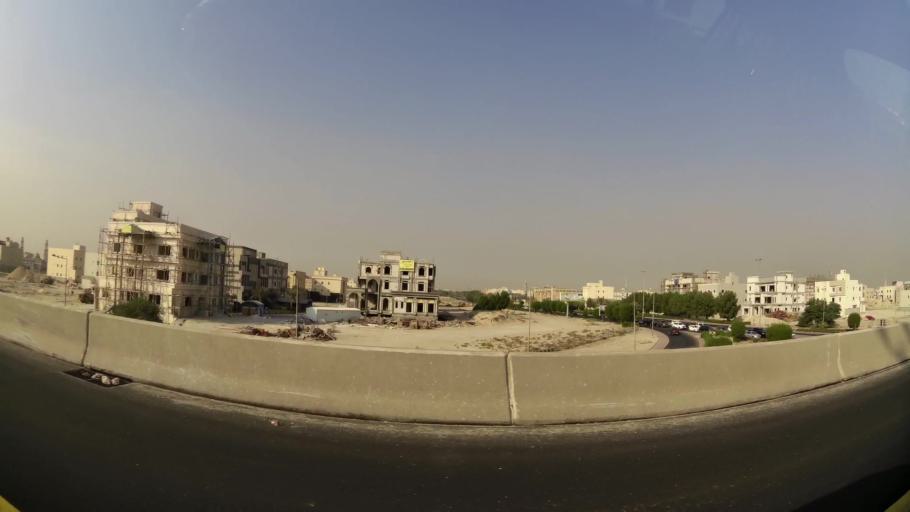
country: KW
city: Al Funaytis
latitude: 29.2120
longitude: 48.1034
